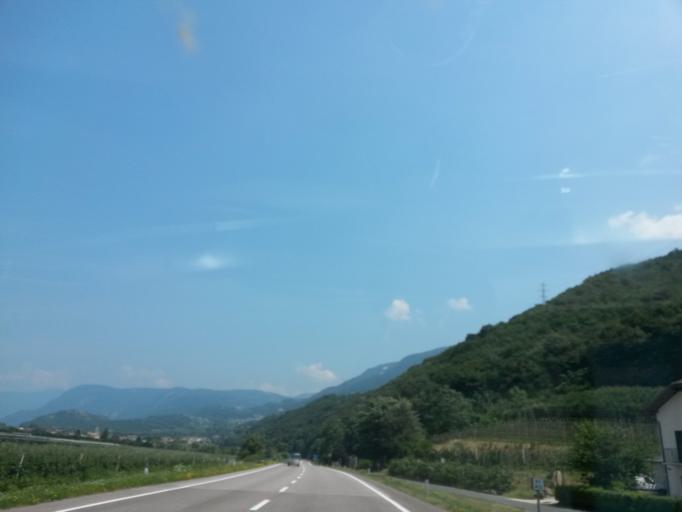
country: IT
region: Trentino-Alto Adige
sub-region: Bolzano
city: Egna
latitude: 46.3015
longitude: 11.2610
